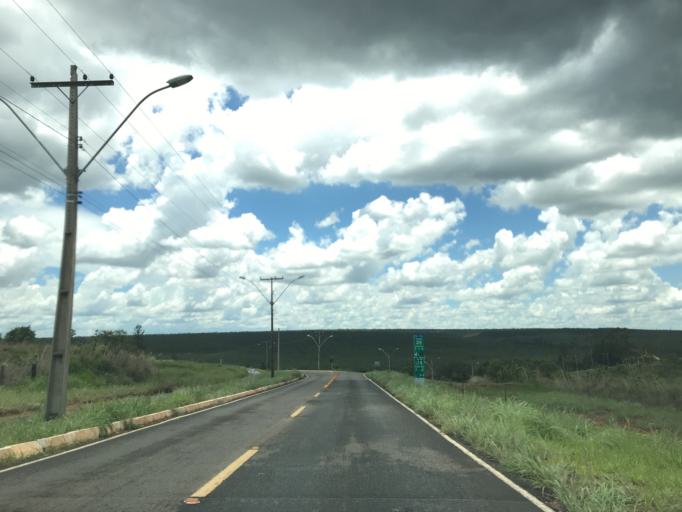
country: BR
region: Federal District
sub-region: Brasilia
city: Brasilia
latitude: -15.9010
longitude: -47.9174
